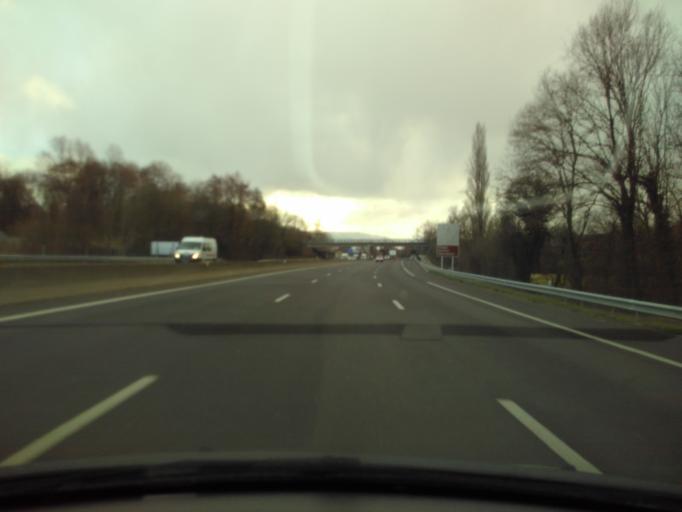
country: FR
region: Rhone-Alpes
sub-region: Departement de la Savoie
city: La Ravoire
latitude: 45.5509
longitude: 5.9581
